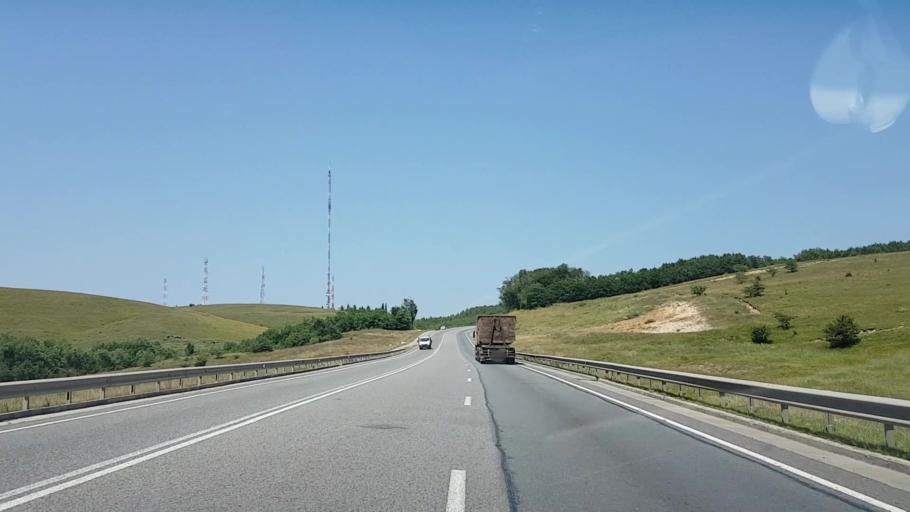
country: RO
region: Cluj
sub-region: Comuna Feleacu
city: Feleacu
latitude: 46.7030
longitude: 23.6416
